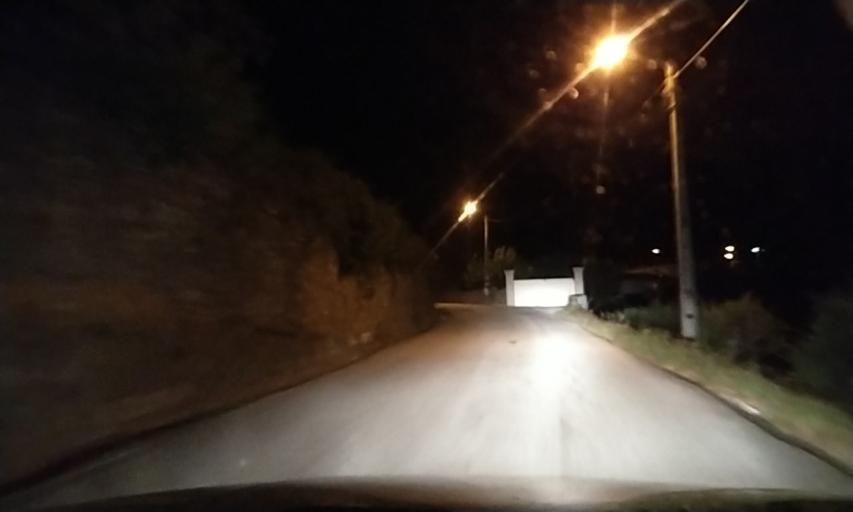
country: PT
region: Vila Real
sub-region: Peso da Regua
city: Godim
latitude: 41.1733
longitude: -7.8146
